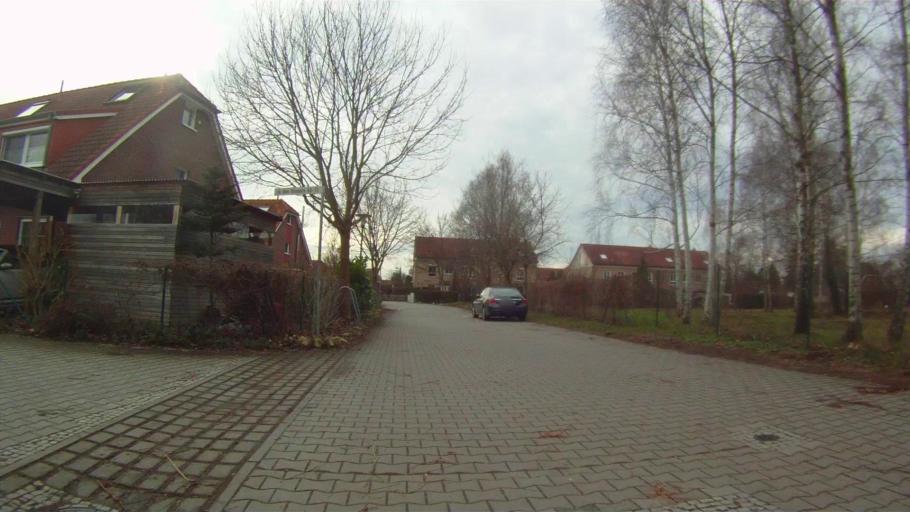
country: DE
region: Berlin
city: Lichtenrade
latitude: 52.3720
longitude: 13.3962
